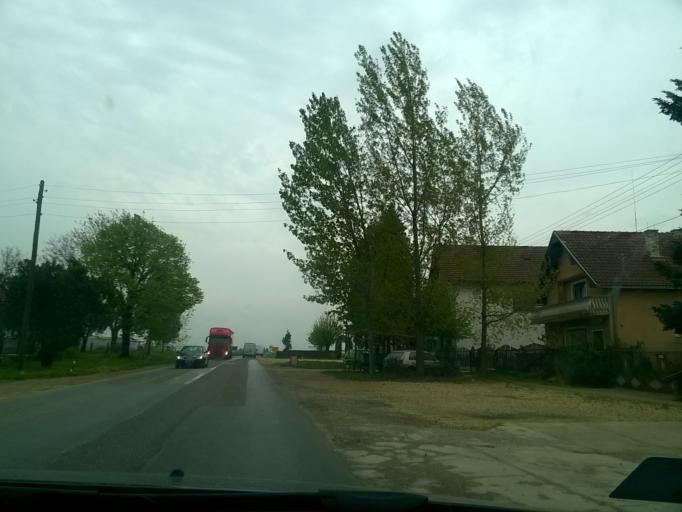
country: RS
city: Hrtkovci
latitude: 44.8687
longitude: 19.7707
